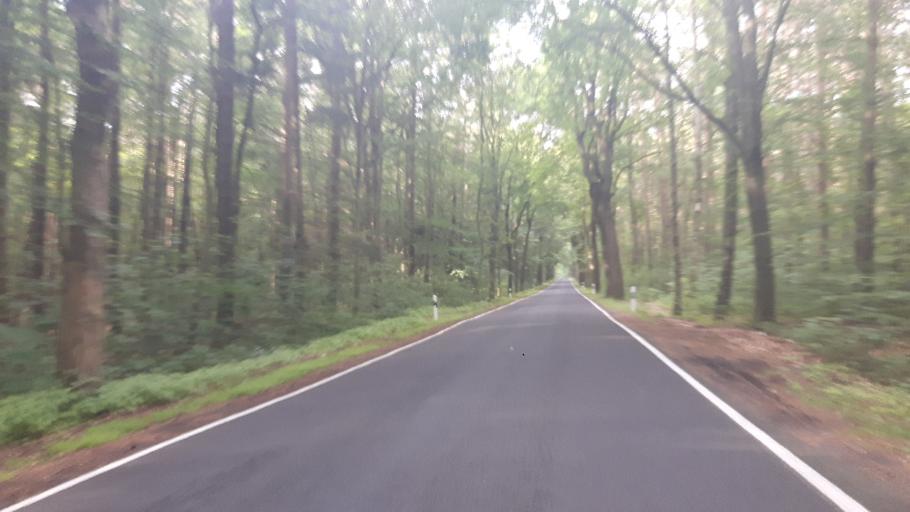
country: DE
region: Brandenburg
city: Hohenfinow
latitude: 52.7862
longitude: 13.8984
